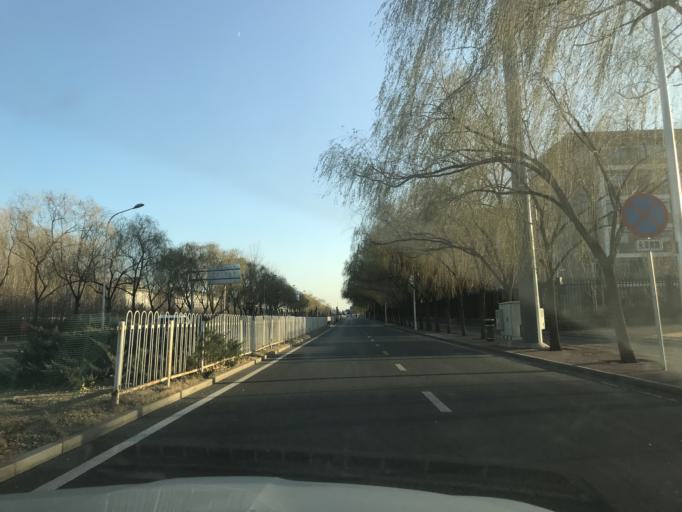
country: CN
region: Beijing
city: Xibeiwang
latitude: 40.0727
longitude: 116.2492
